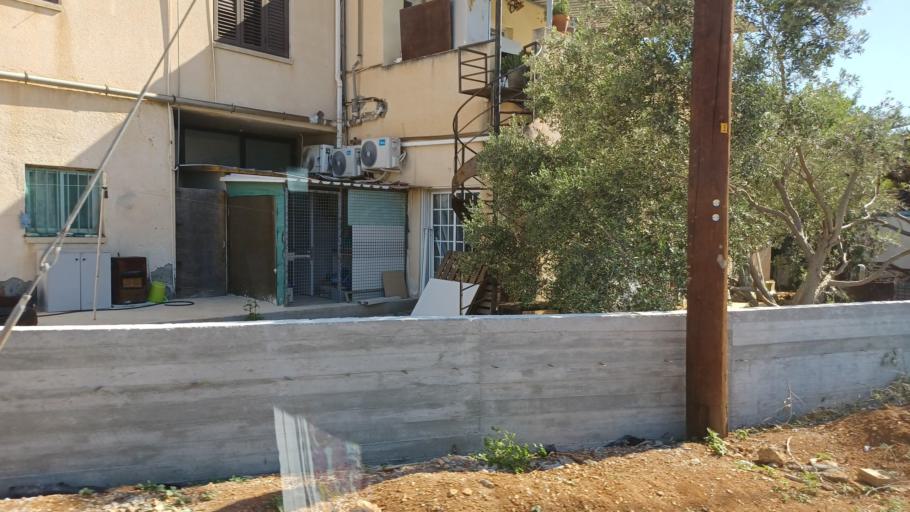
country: CY
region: Lefkosia
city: Kokkinotrimithia
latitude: 35.1486
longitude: 33.2133
